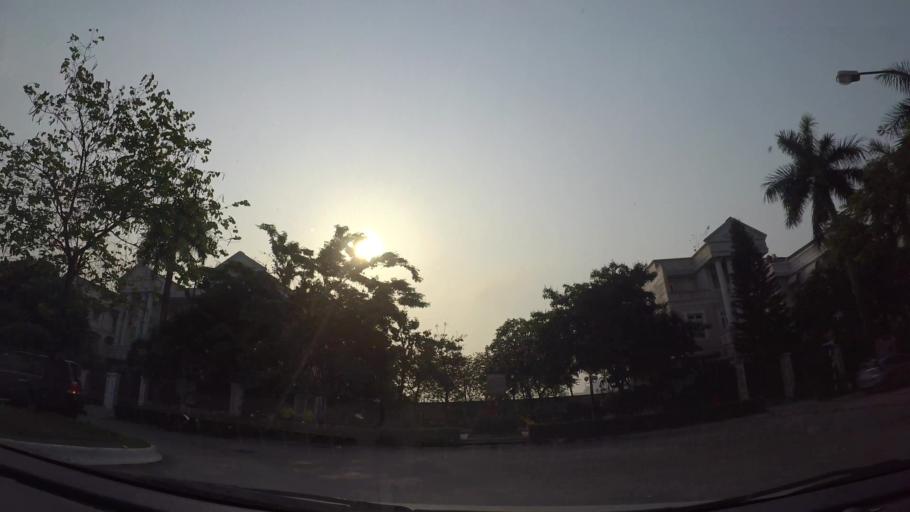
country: VN
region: Ha Noi
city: Tay Ho
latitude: 21.0751
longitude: 105.8051
